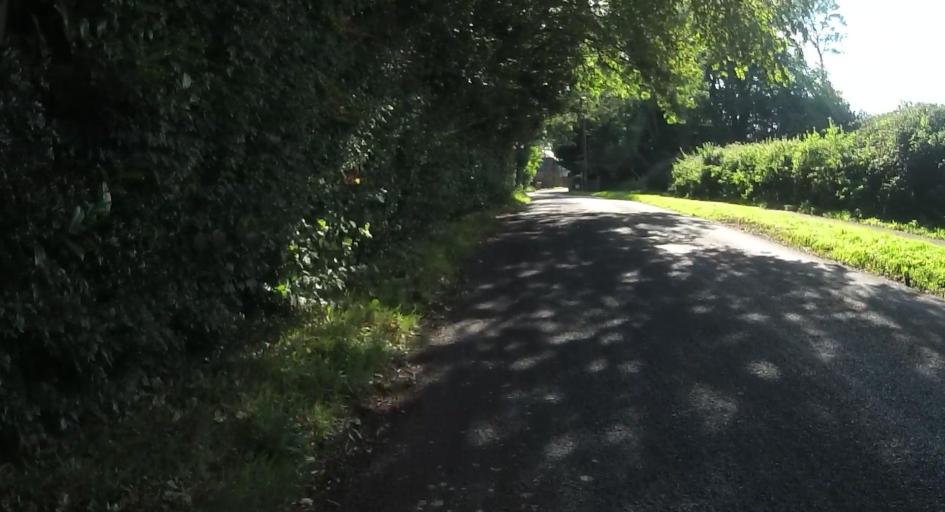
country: GB
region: England
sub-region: Hampshire
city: Four Marks
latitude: 51.1590
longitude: -1.0453
